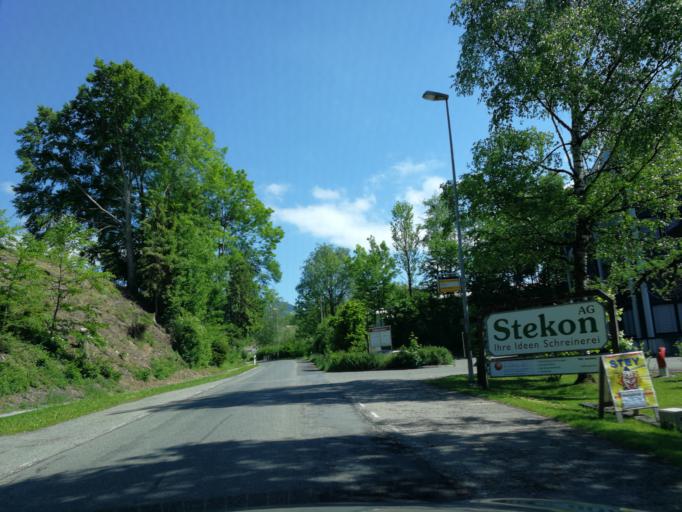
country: CH
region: Saint Gallen
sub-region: Wahlkreis See-Gaster
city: Eschenbach
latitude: 47.2348
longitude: 8.9257
